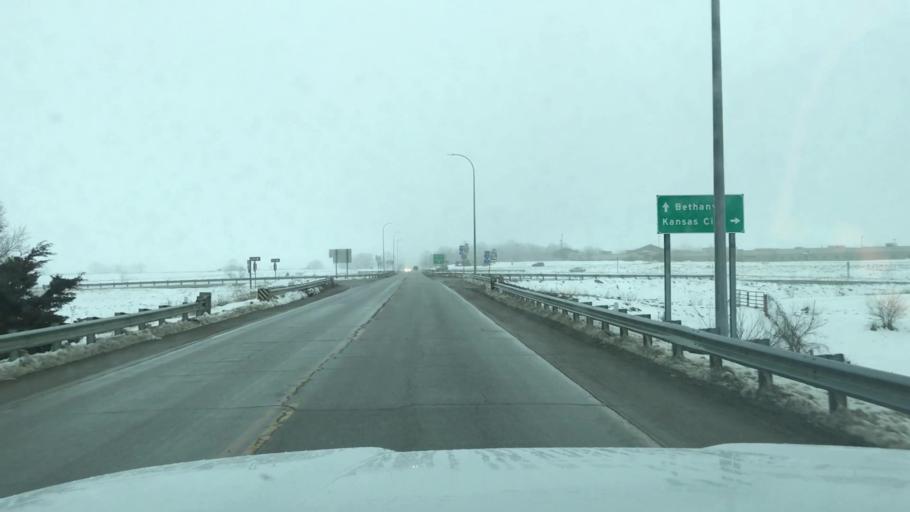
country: US
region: Missouri
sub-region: Clinton County
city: Cameron
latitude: 39.7317
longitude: -94.2226
